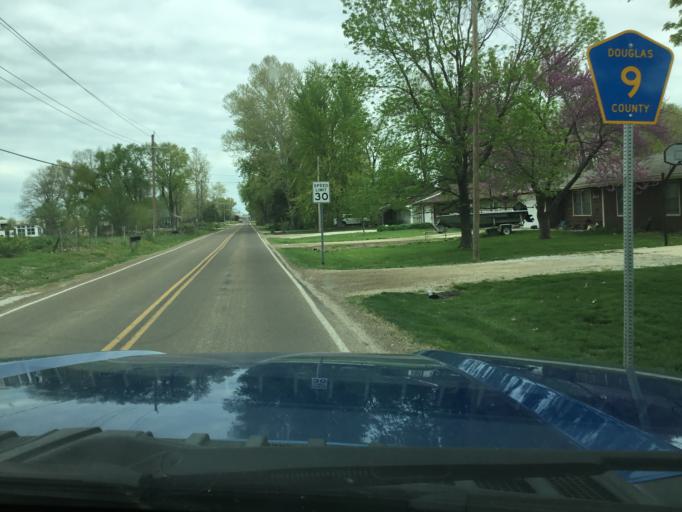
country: US
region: Kansas
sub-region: Douglas County
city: Lawrence
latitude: 38.9861
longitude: -95.2240
